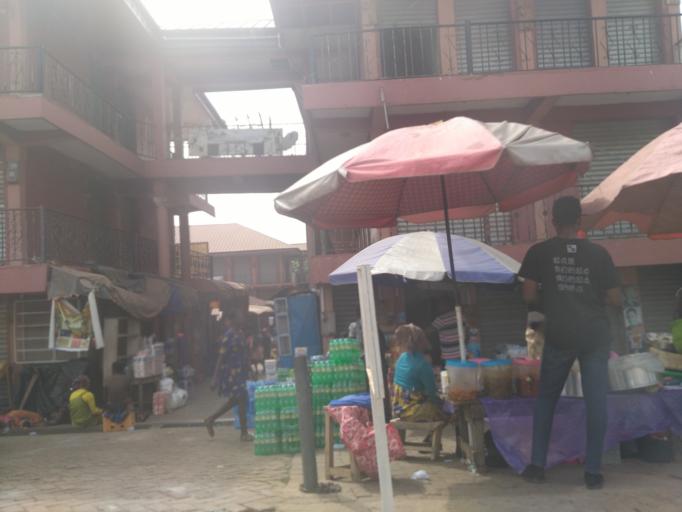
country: GH
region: Ashanti
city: Kumasi
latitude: 6.7046
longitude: -1.6249
